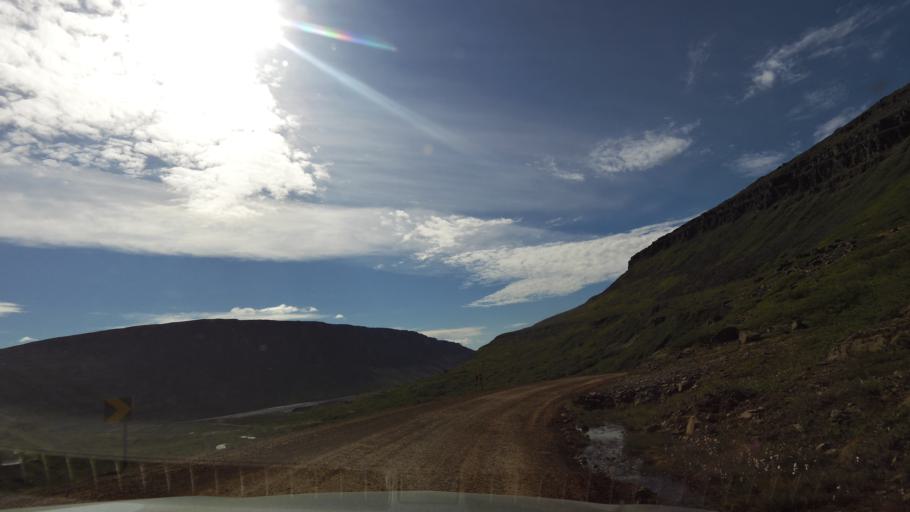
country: IS
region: Westfjords
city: Isafjoerdur
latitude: 65.7516
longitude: -23.1828
